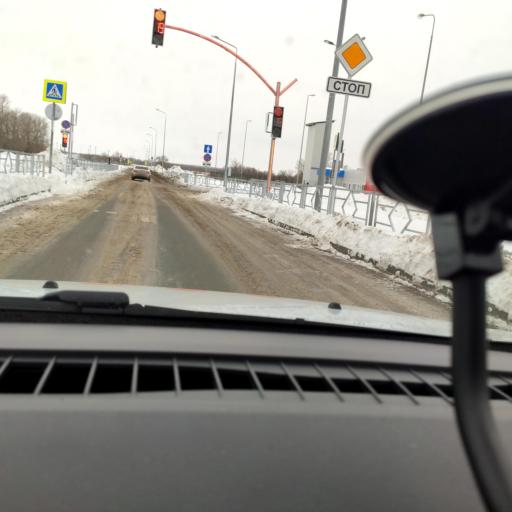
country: RU
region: Samara
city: Samara
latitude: 53.0910
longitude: 50.1601
